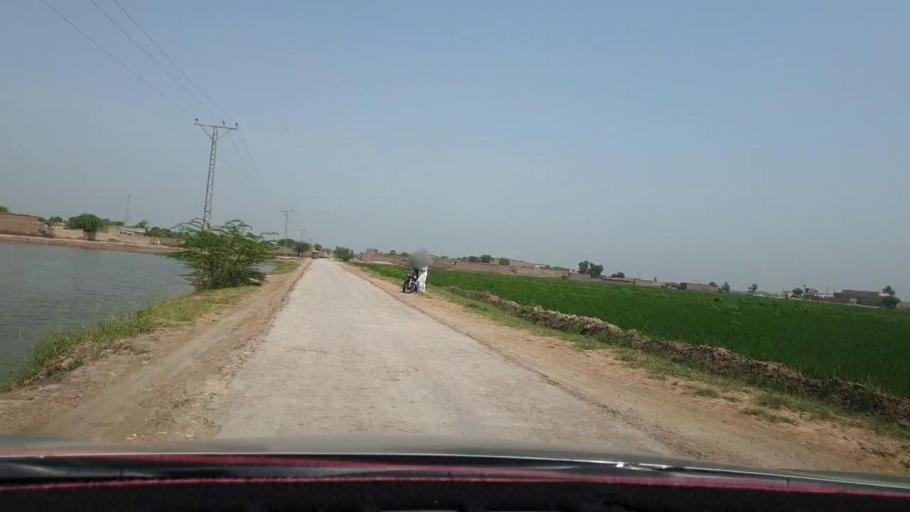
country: PK
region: Sindh
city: Warah
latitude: 27.4417
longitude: 67.7752
